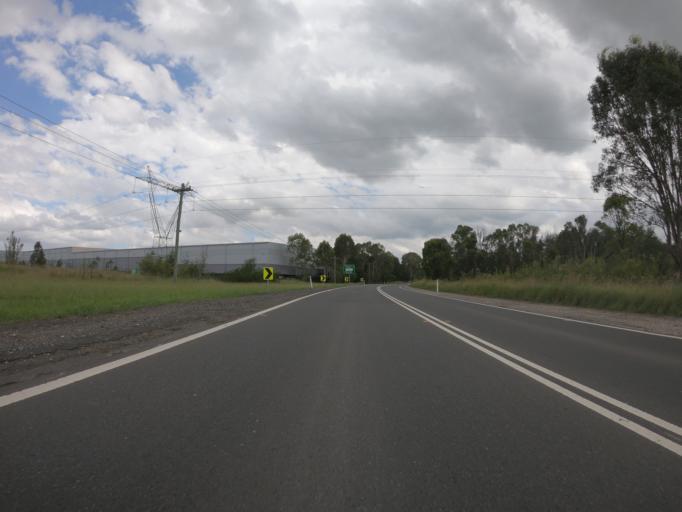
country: AU
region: New South Wales
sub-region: Blacktown
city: Mount Druitt
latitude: -33.8122
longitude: 150.7756
